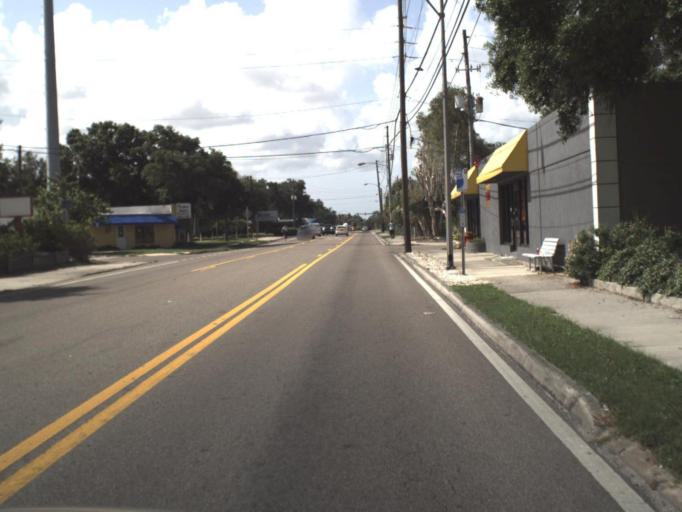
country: US
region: Florida
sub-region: Pinellas County
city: Belleair
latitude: 27.9479
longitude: -82.8000
